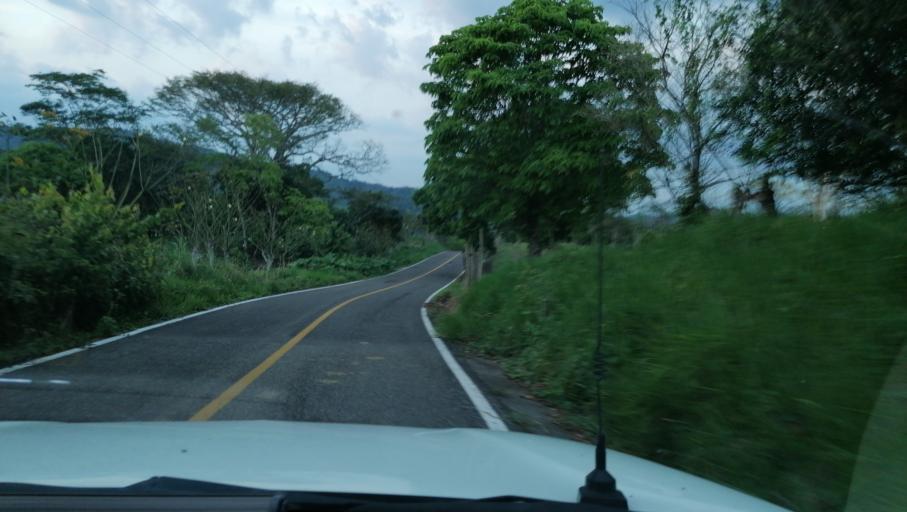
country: MX
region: Chiapas
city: Pichucalco
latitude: 17.5246
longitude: -93.1535
